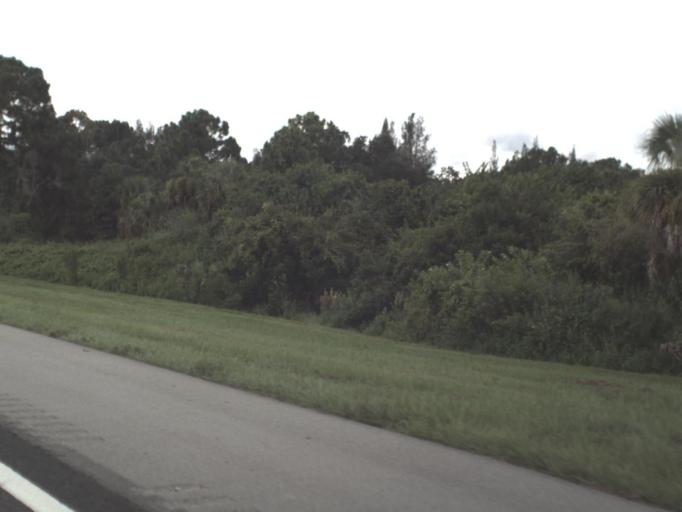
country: US
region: Florida
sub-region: Sarasota County
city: Venice Gardens
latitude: 27.1179
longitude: -82.3928
